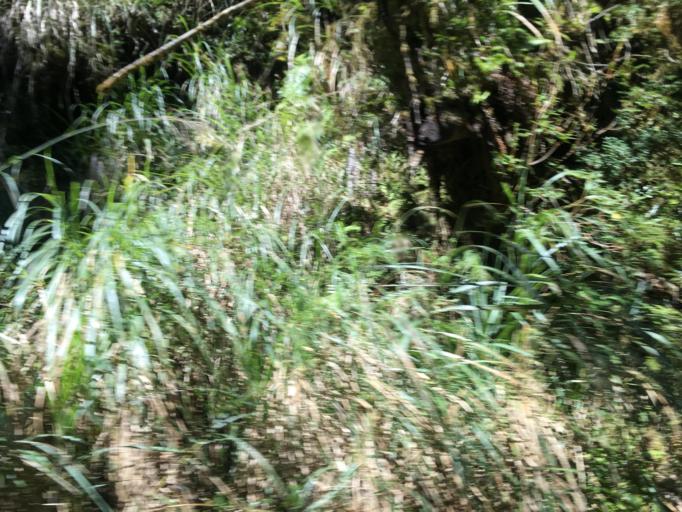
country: TW
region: Taiwan
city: Daxi
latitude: 24.5726
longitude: 121.4148
